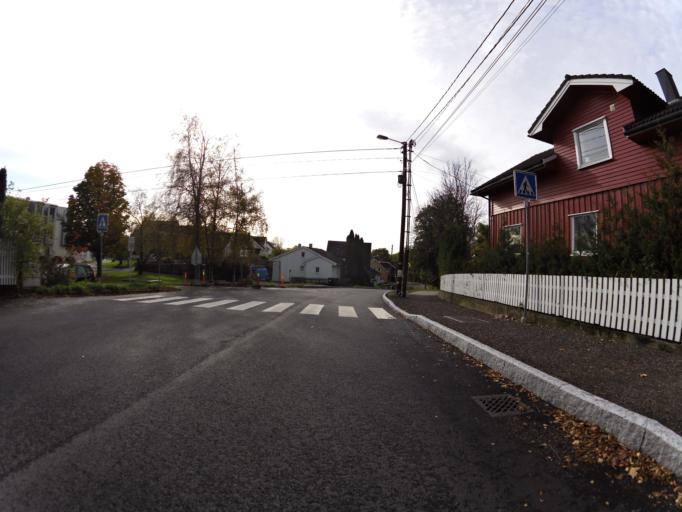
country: NO
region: Ostfold
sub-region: Fredrikstad
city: Fredrikstad
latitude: 59.2217
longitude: 10.9452
